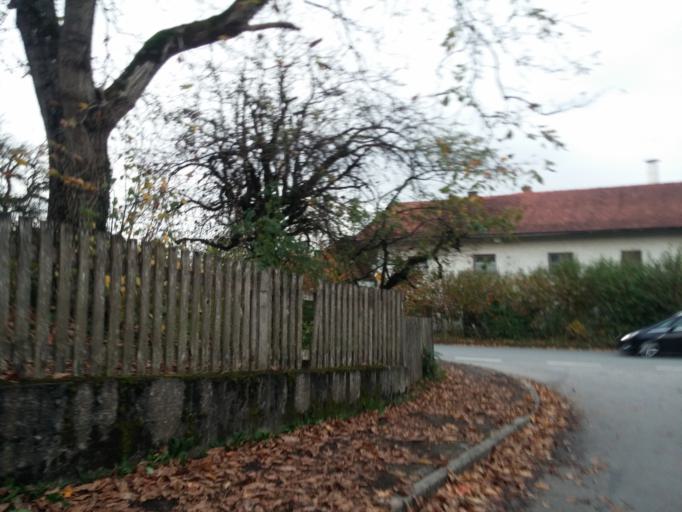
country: DE
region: Bavaria
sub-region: Upper Bavaria
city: Grafing bei Munchen
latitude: 48.0260
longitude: 11.9924
